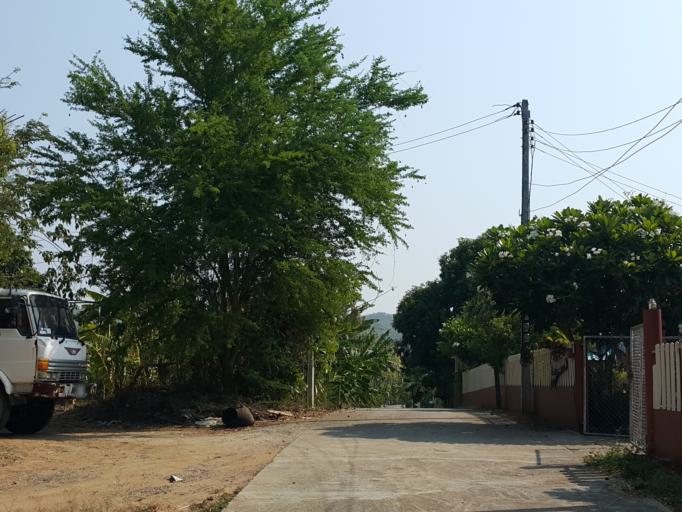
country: TH
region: Kanchanaburi
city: Sai Yok
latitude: 14.1105
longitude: 99.1357
